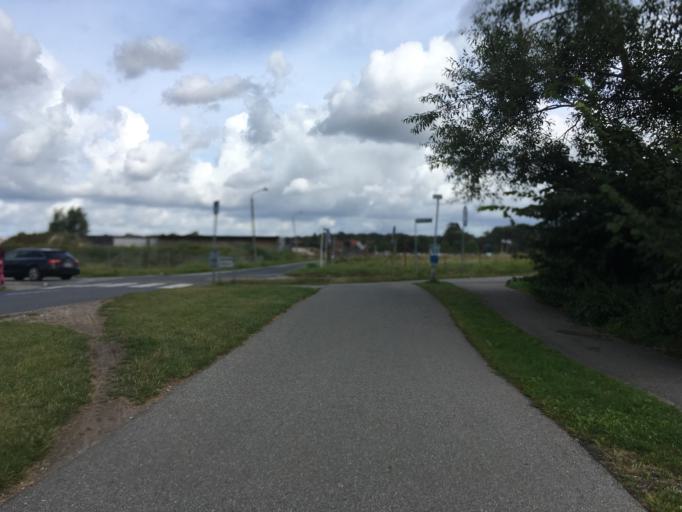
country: DK
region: Capital Region
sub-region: Hillerod Kommune
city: Hillerod
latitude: 55.9287
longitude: 12.2864
